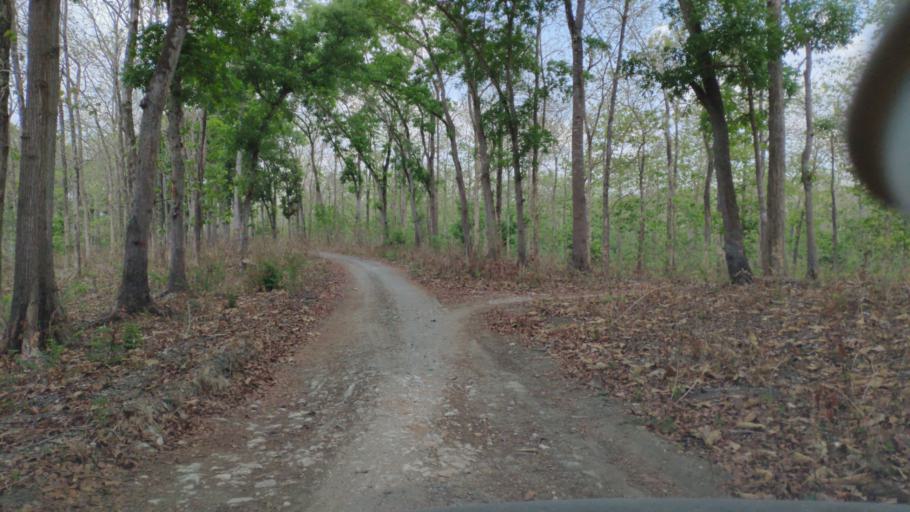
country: ID
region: Central Java
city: Singonegoro
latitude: -6.9922
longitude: 111.5334
